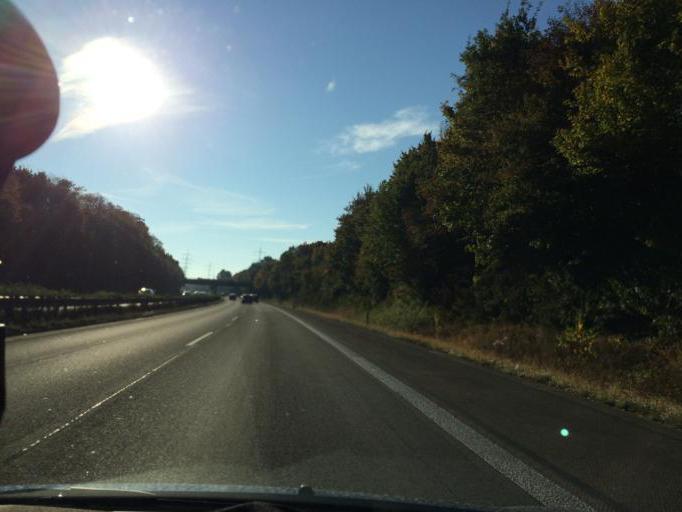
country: DE
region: North Rhine-Westphalia
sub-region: Regierungsbezirk Koln
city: Wahn-Heide
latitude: 50.8274
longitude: 7.0965
